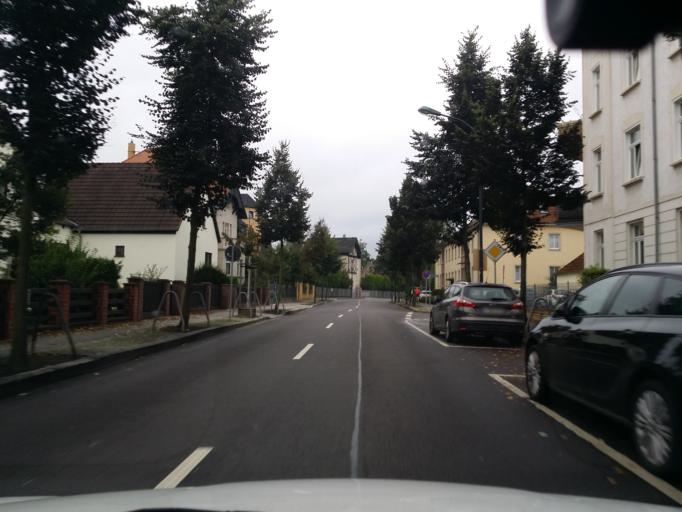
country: DE
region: Saxony
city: Markkleeberg
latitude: 51.2764
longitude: 12.3768
